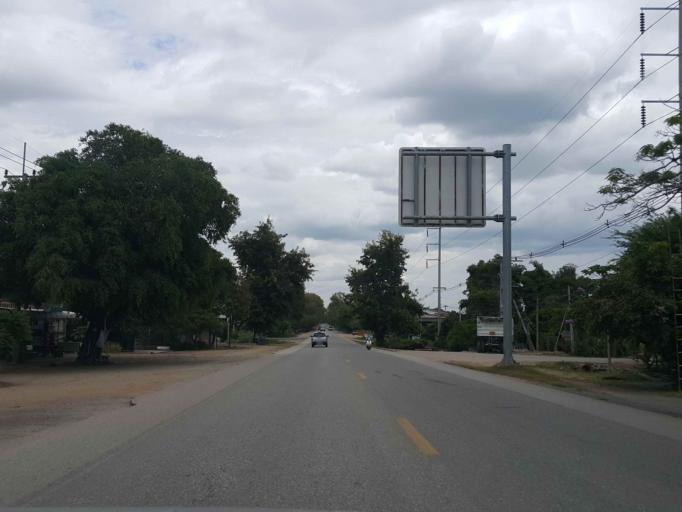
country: TH
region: Chiang Mai
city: Doi Lo
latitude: 18.4283
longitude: 98.8649
